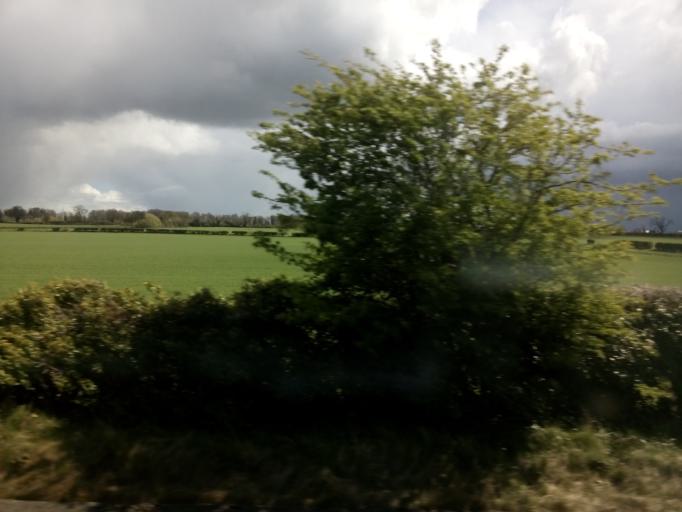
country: GB
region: Scotland
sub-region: East Lothian
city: Longniddry
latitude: 55.9713
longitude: -2.8997
